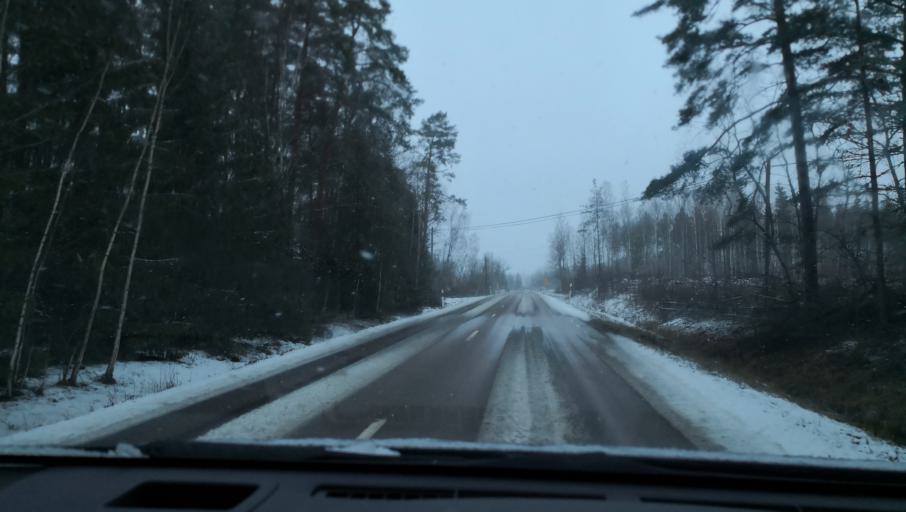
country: SE
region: Vaestmanland
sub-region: Hallstahammars Kommun
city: Kolback
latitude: 59.5908
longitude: 16.3556
